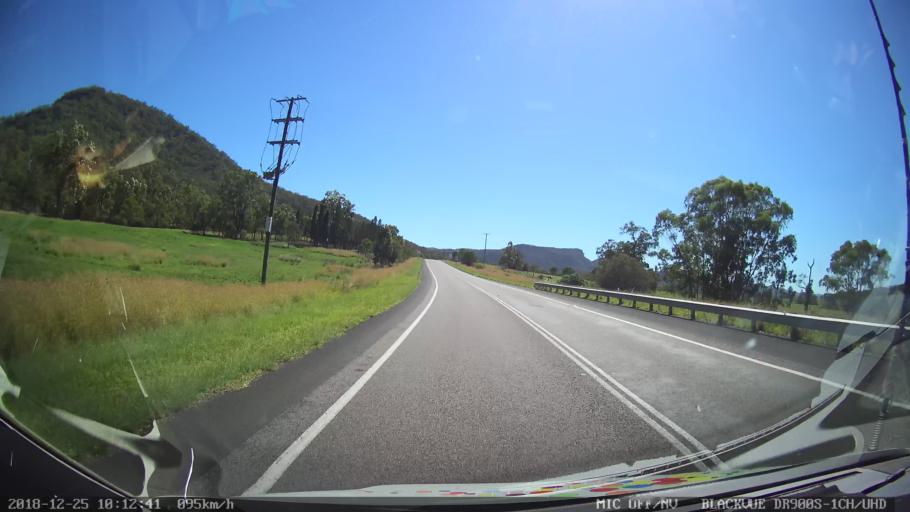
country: AU
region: New South Wales
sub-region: Muswellbrook
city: Denman
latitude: -32.3286
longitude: 150.5344
